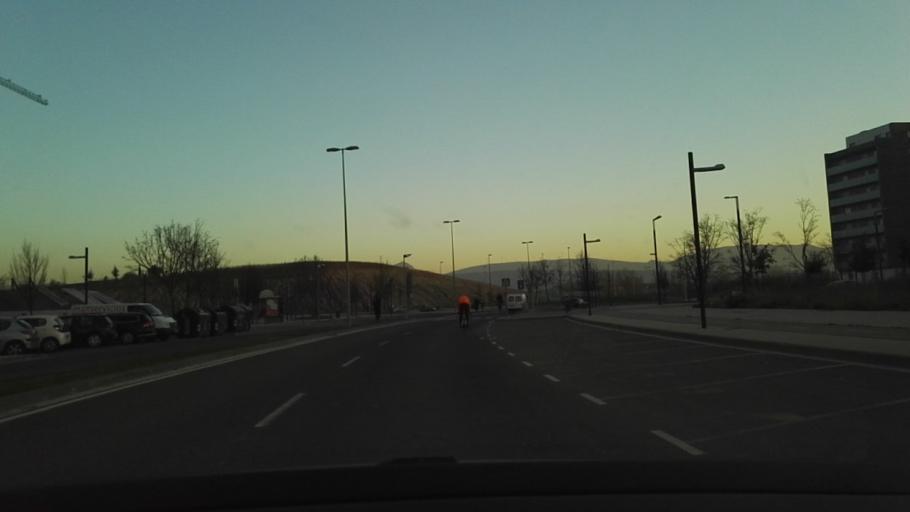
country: ES
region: Navarre
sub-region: Provincia de Navarra
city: Segundo Ensanche
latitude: 42.8036
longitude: -1.6271
